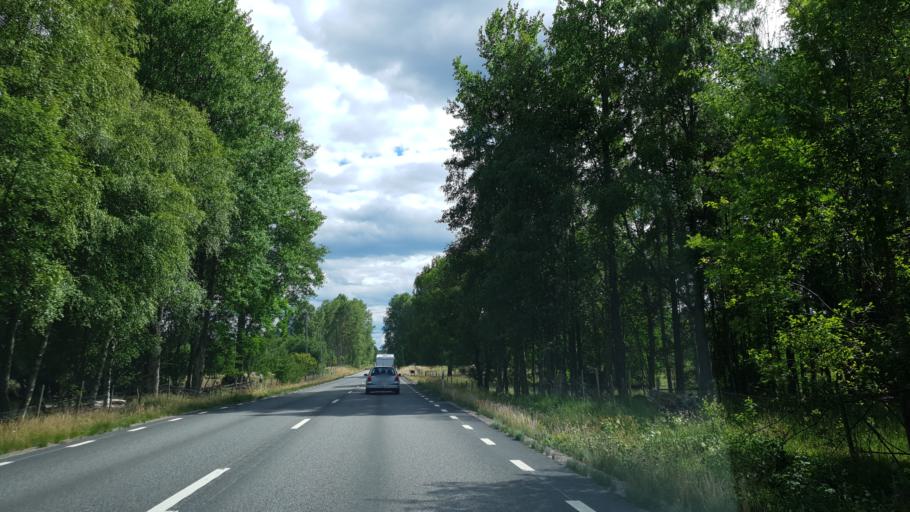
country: SE
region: Kronoberg
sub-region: Lessebo Kommun
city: Lessebo
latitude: 56.7954
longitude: 15.4125
